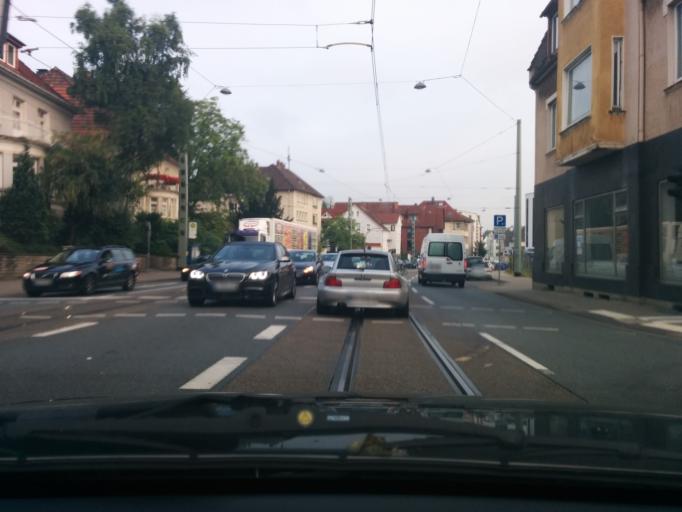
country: DE
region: North Rhine-Westphalia
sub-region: Regierungsbezirk Detmold
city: Bielefeld
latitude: 52.0108
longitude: 8.5398
